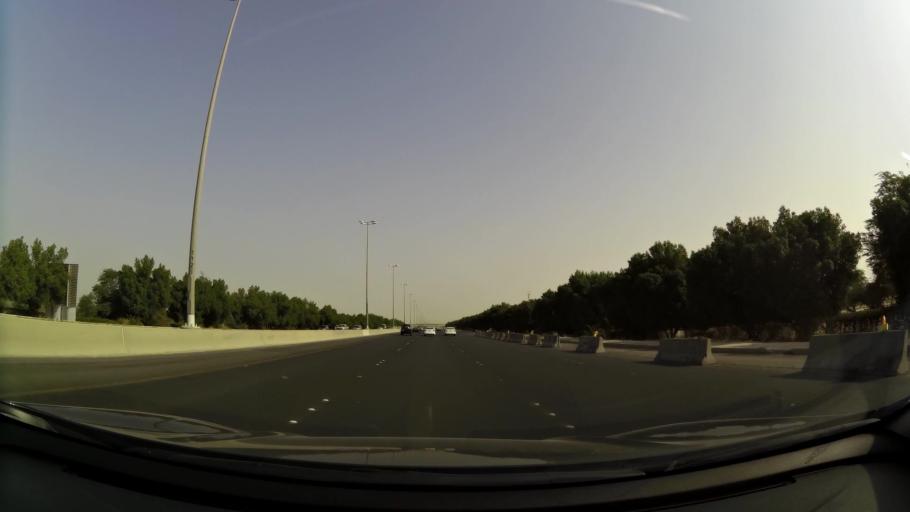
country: KW
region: Muhafazat al Jahra'
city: Al Jahra'
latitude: 29.3347
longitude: 47.7277
